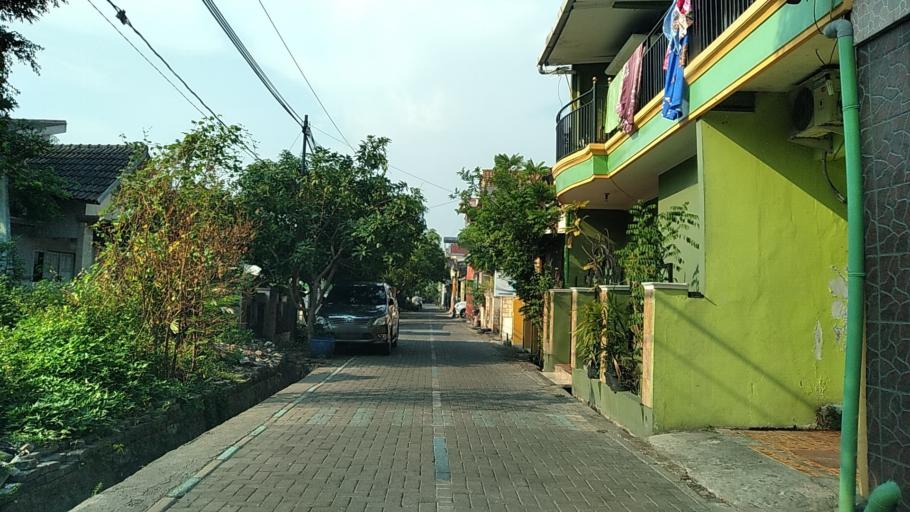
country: ID
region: Central Java
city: Semarang
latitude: -7.0058
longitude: 110.4577
